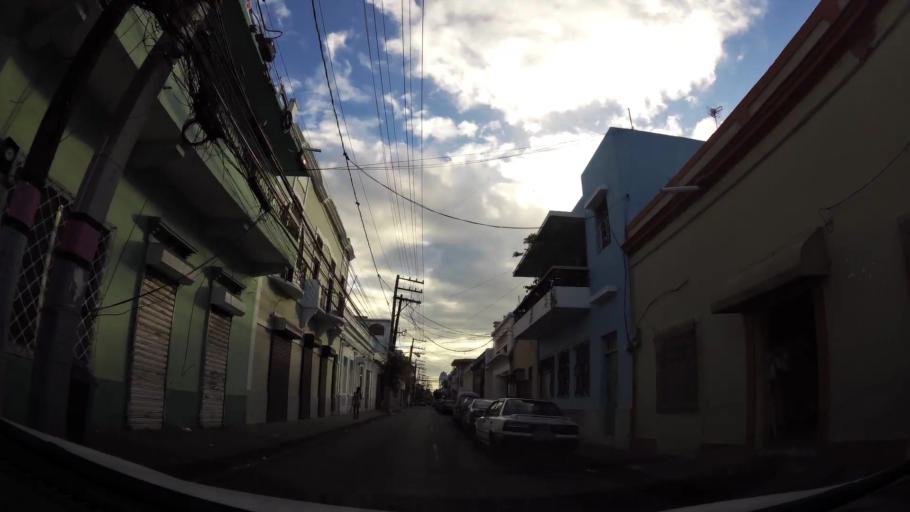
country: DO
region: Nacional
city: Ciudad Nueva
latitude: 18.4699
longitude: -69.8896
